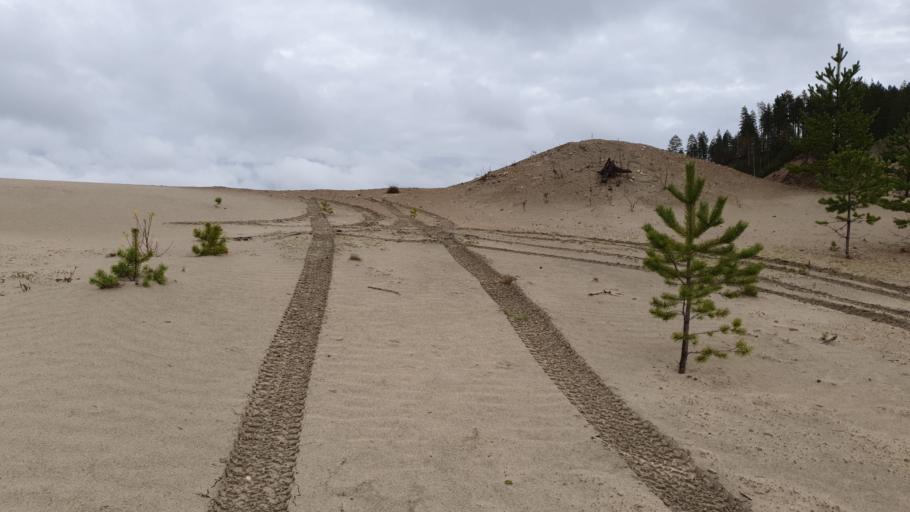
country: FI
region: Kainuu
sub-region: Kehys-Kainuu
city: Kuhmo
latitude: 64.1501
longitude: 29.4011
